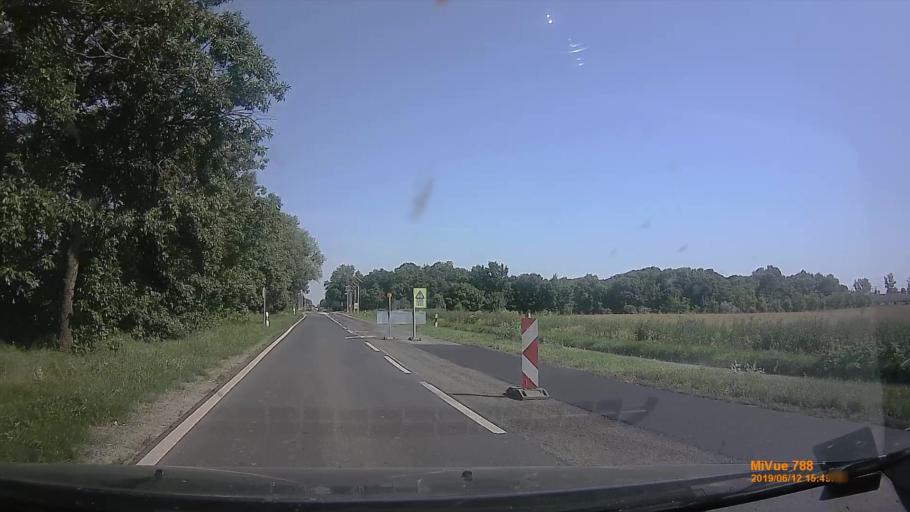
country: HU
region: Csongrad
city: Apatfalva
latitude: 46.1981
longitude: 20.5554
